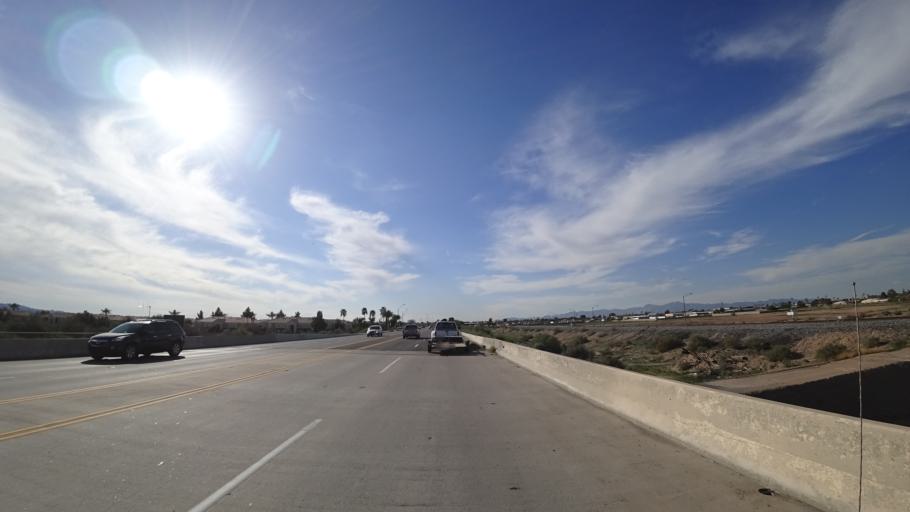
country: US
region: Arizona
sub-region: Maricopa County
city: Avondale
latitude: 33.4351
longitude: -112.3339
